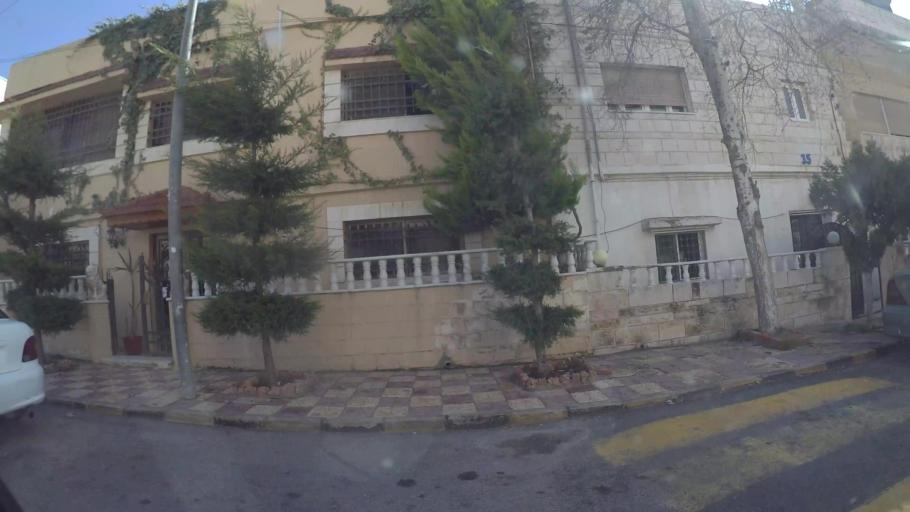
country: JO
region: Amman
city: Al Jubayhah
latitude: 32.0183
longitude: 35.8542
